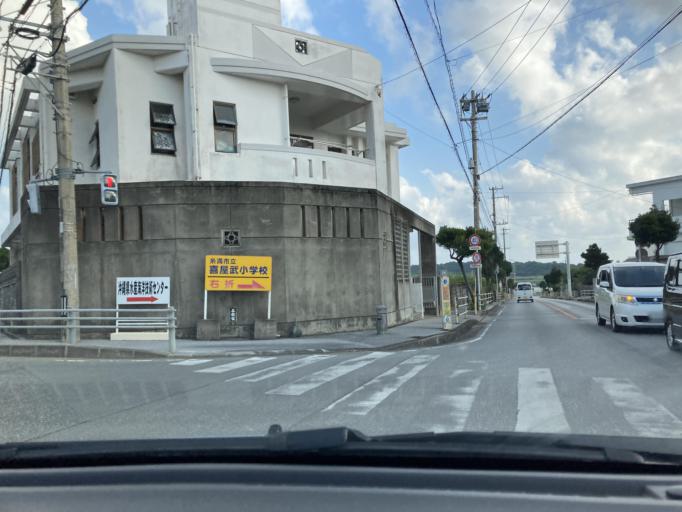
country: JP
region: Okinawa
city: Itoman
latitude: 26.1048
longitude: 127.6666
